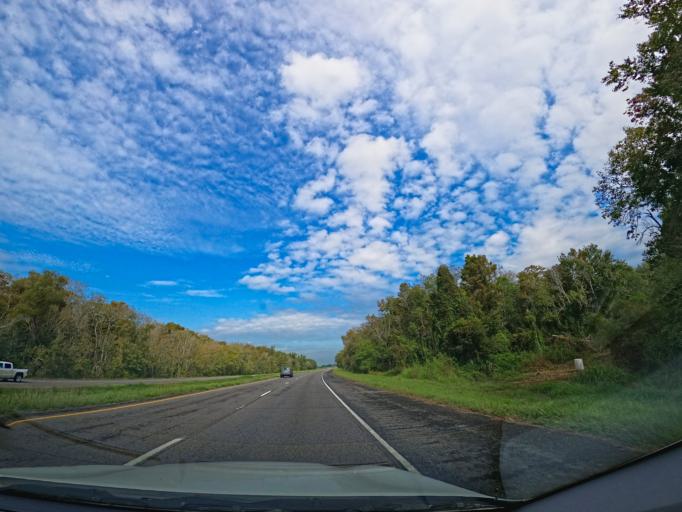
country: US
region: Louisiana
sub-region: Saint Mary Parish
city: Patterson
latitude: 29.7200
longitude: -91.4074
